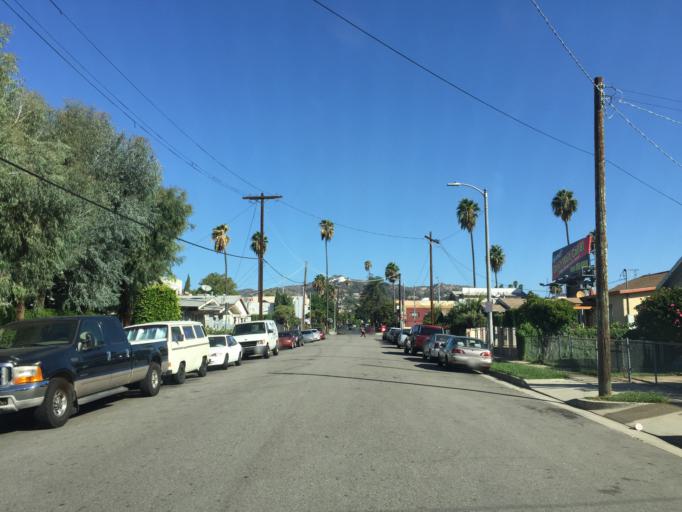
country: US
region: California
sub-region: Los Angeles County
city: Hollywood
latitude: 34.0972
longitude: -118.2994
